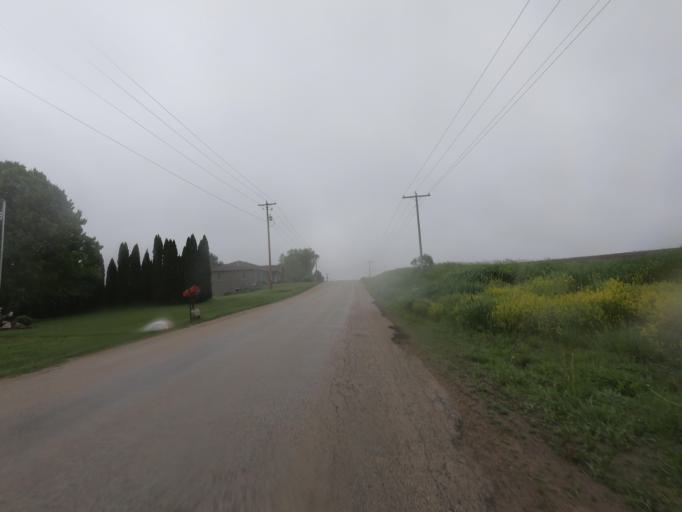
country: US
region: Wisconsin
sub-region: Grant County
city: Hazel Green
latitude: 42.5076
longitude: -90.4984
